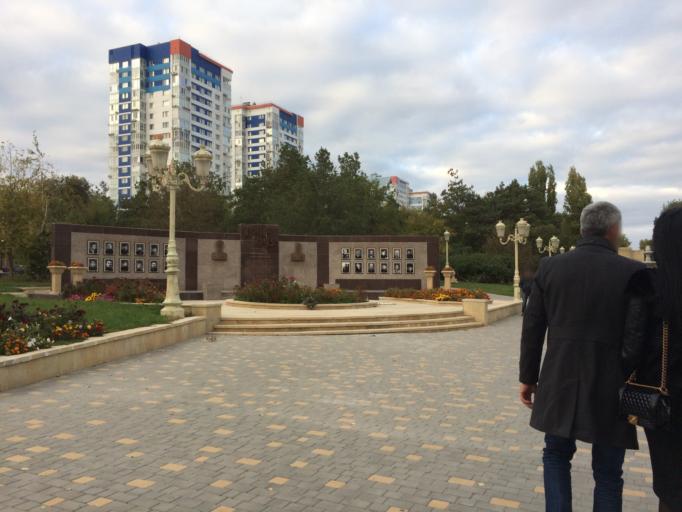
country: RU
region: Volgograd
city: Krasnoslobodsk
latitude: 48.7268
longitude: 44.5423
